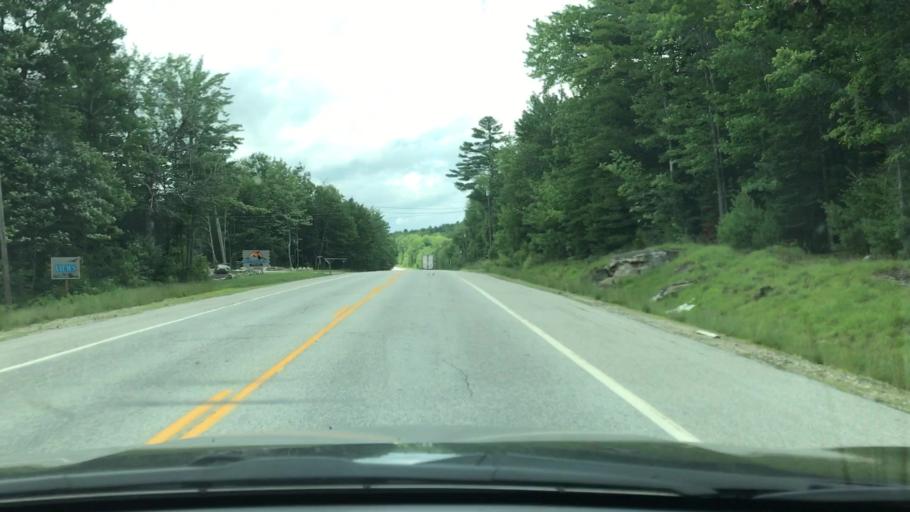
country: US
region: Maine
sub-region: Oxford County
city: West Paris
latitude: 44.3642
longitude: -70.5885
